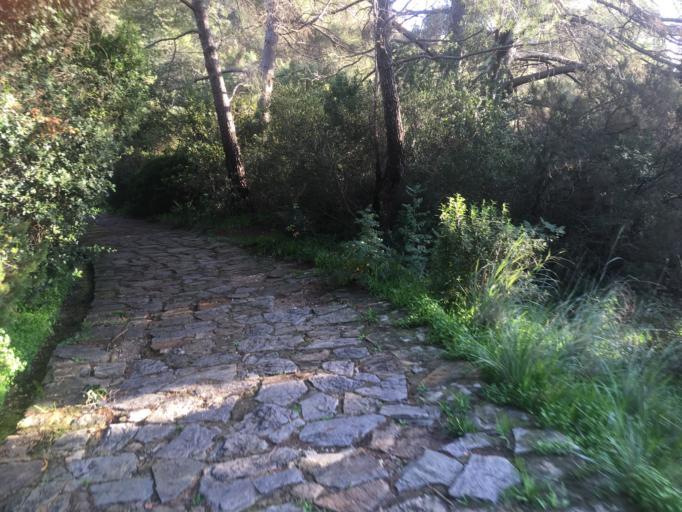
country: FR
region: Provence-Alpes-Cote d'Azur
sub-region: Departement du Var
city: Cavalaire-sur-Mer
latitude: 43.1550
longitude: 6.4822
